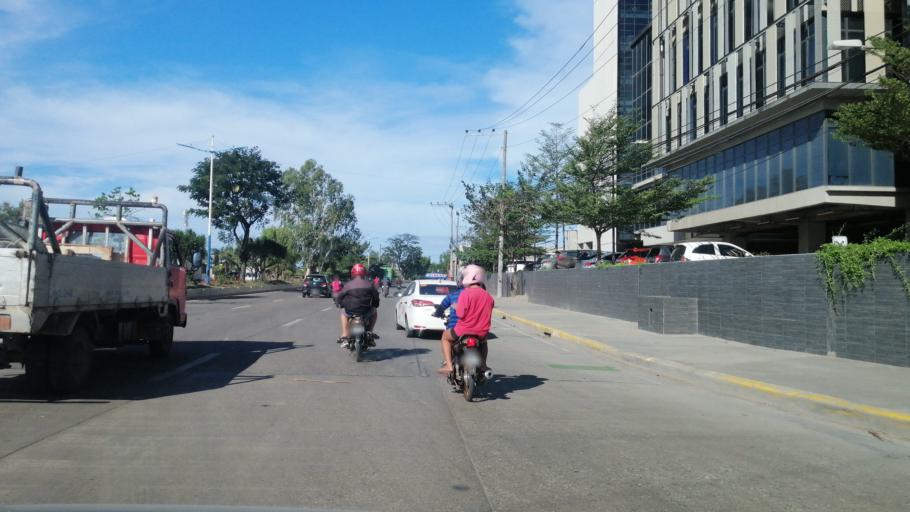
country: PH
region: Central Visayas
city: Mandaue City
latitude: 10.3249
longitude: 123.9363
